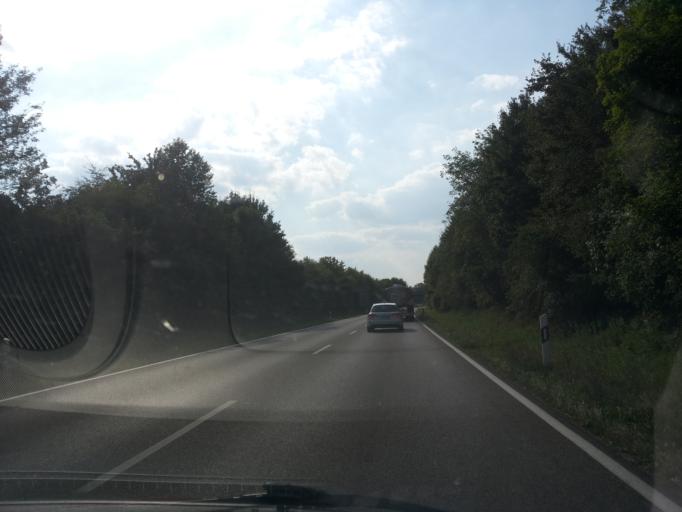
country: DE
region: Bavaria
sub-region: Upper Bavaria
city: Weichering
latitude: 48.7116
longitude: 11.3203
